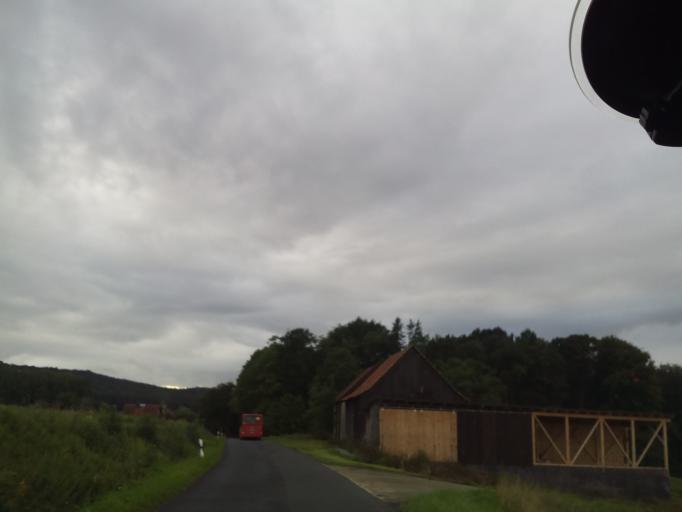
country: DE
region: Bavaria
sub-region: Regierungsbezirk Unterfranken
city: Pfarrweisach
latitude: 50.1914
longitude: 10.7689
